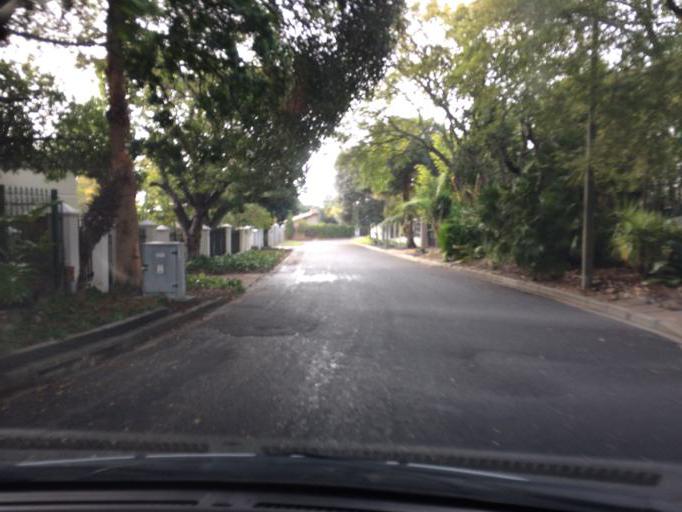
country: ZA
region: Western Cape
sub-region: City of Cape Town
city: Kraaifontein
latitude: -33.8625
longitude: 18.6471
